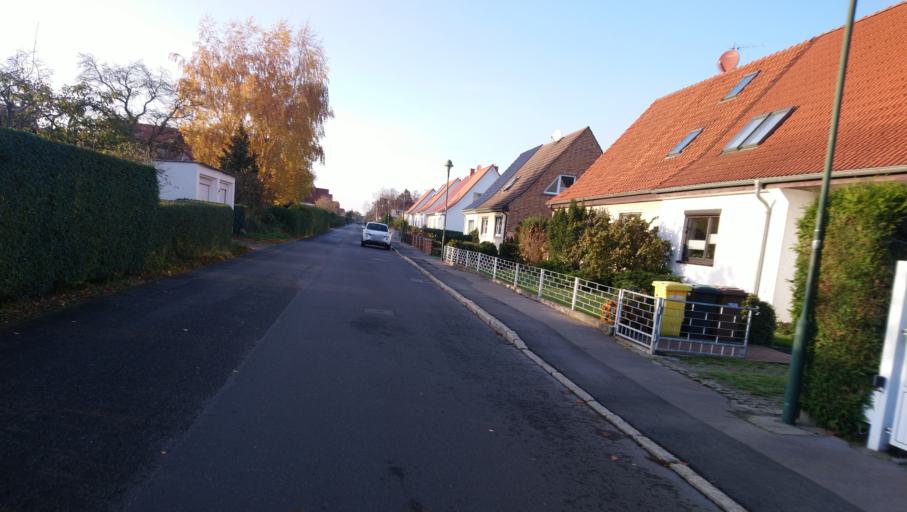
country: DE
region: Mecklenburg-Vorpommern
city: Rostock
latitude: 54.1013
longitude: 12.0873
